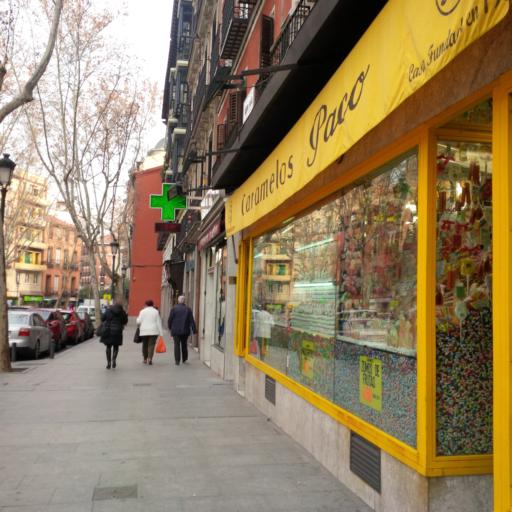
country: ES
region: Madrid
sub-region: Provincia de Madrid
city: Madrid
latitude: 40.4116
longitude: -3.7080
